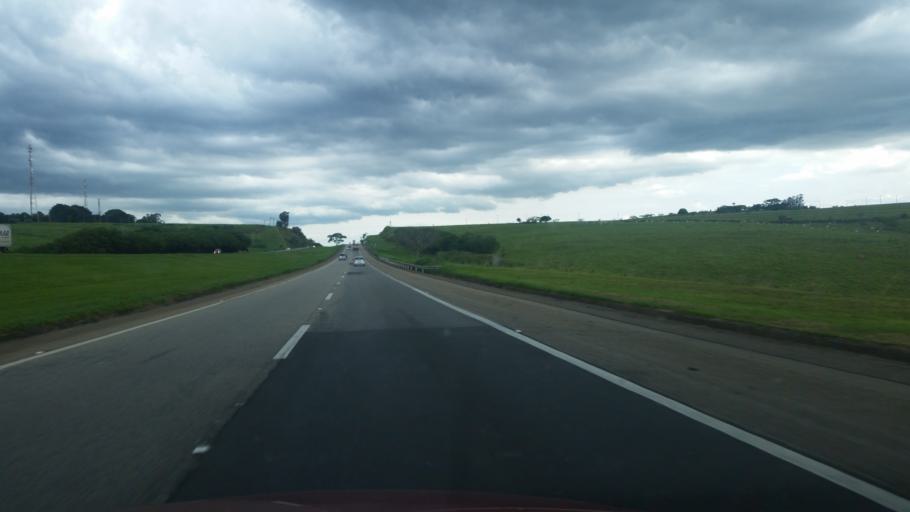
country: BR
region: Sao Paulo
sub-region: Boituva
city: Boituva
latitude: -23.3191
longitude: -47.6079
